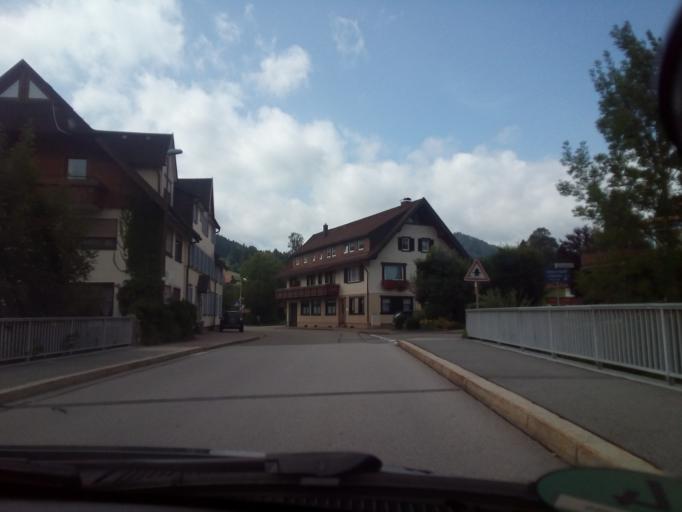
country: DE
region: Baden-Wuerttemberg
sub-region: Karlsruhe Region
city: Baiersbronn
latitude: 48.5186
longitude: 8.3236
